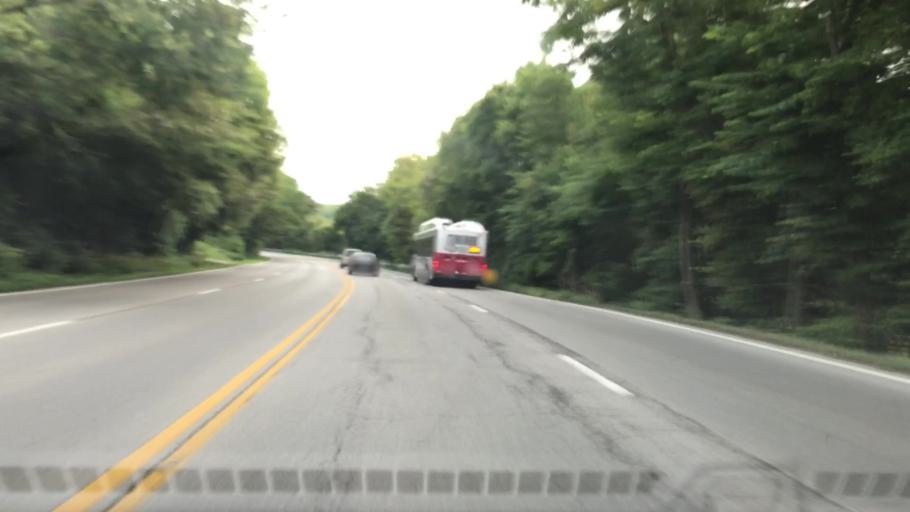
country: US
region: Ohio
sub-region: Franklin County
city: Upper Arlington
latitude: 40.0152
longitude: -83.0906
